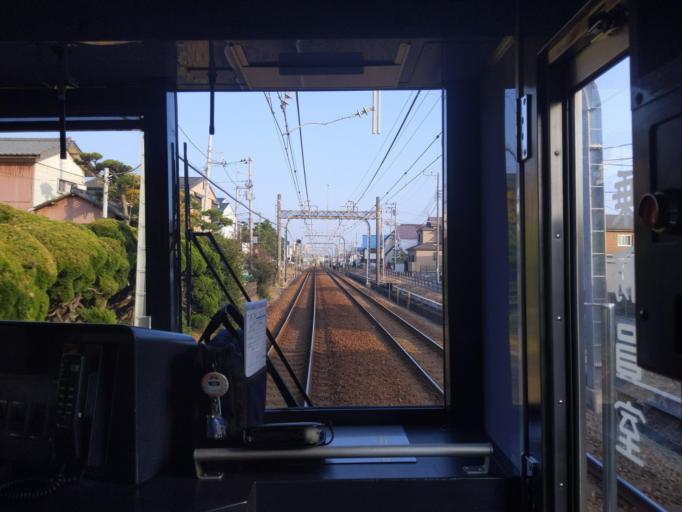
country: JP
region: Kanagawa
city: Fujisawa
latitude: 35.3174
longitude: 139.4743
